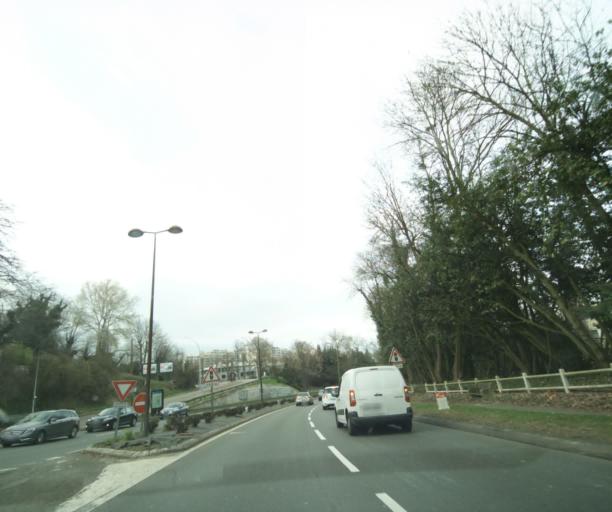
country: FR
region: Ile-de-France
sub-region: Departement des Yvelines
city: Louveciennes
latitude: 48.8738
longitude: 2.1018
